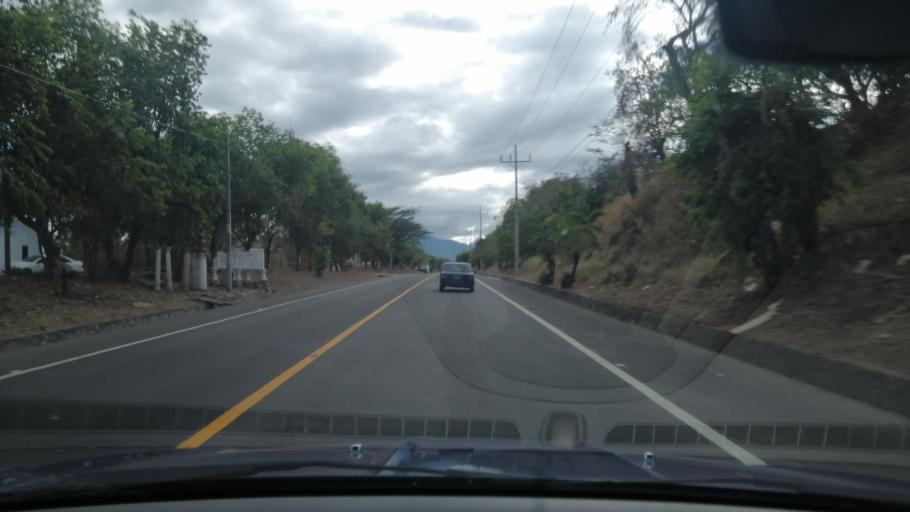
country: SV
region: Santa Ana
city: Santa Ana
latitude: 13.9889
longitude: -89.5435
